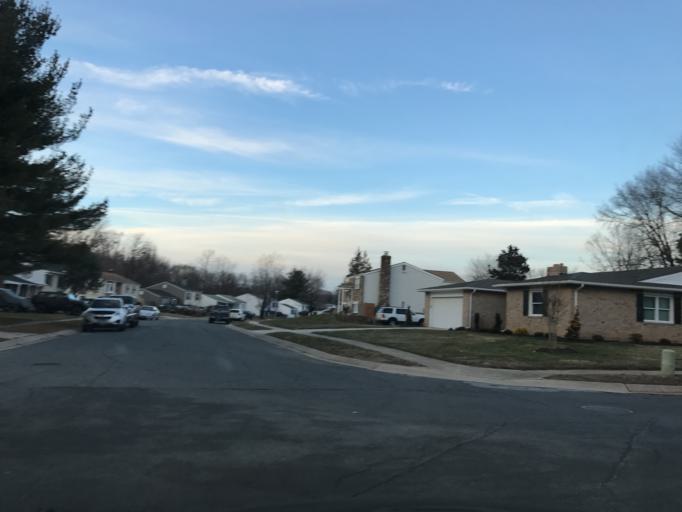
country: US
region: Maryland
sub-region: Harford County
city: Joppatowne
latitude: 39.4064
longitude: -76.3632
